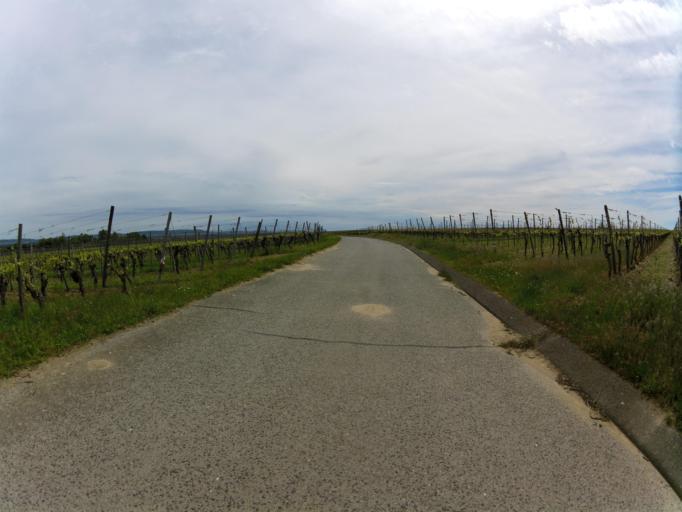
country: DE
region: Bavaria
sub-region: Regierungsbezirk Unterfranken
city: Sommerach
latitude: 49.8473
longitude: 10.2043
